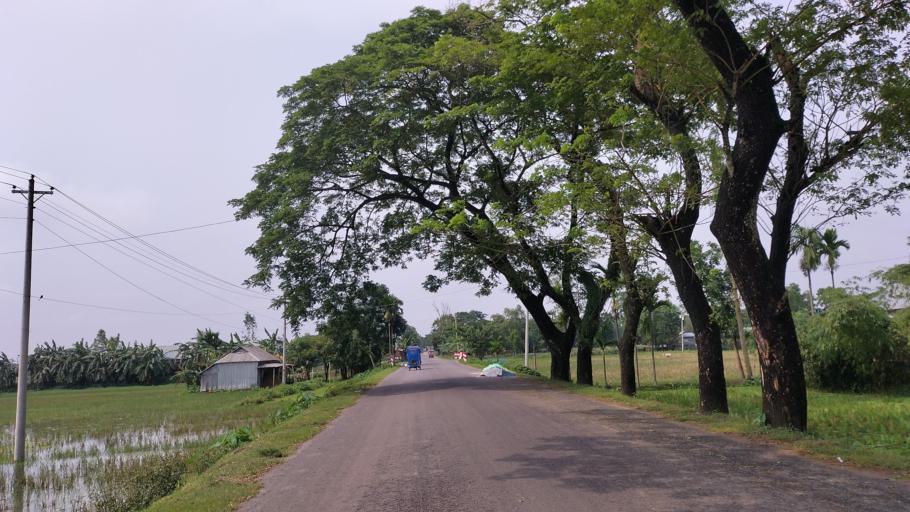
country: BD
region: Dhaka
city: Netrakona
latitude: 24.9480
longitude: 90.8318
